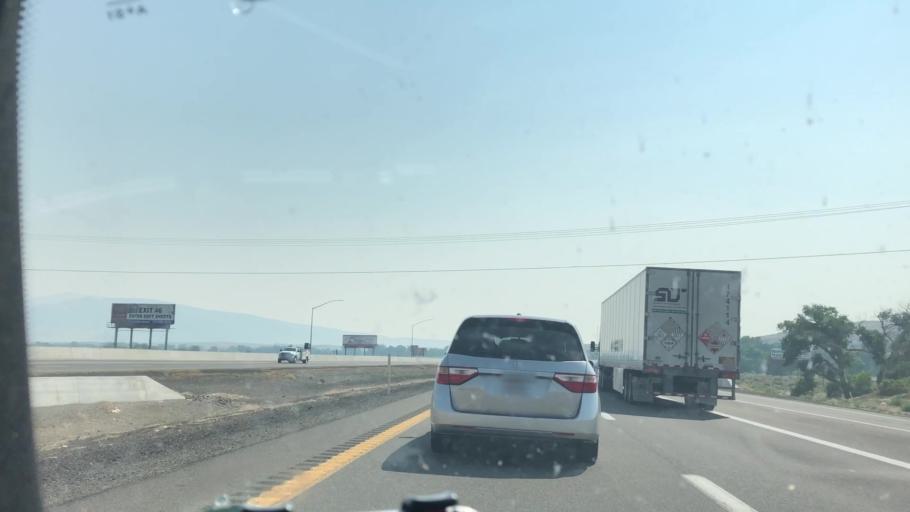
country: US
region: Nevada
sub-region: Lyon County
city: Fernley
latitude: 39.6165
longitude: -119.3068
